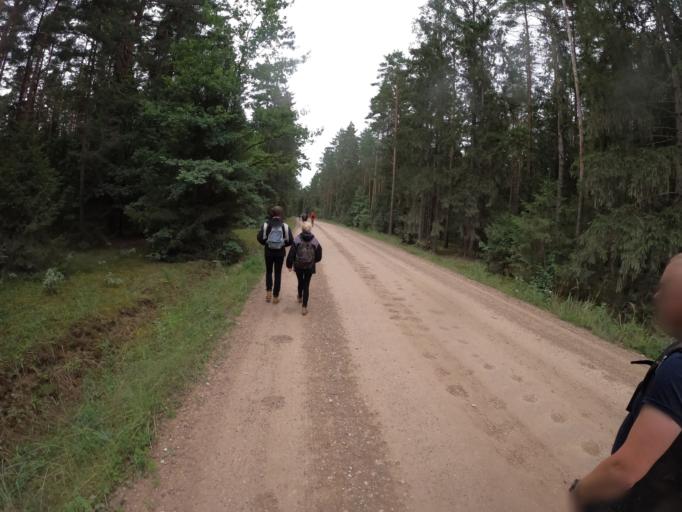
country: LV
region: Kuldigas Rajons
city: Kuldiga
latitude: 56.9892
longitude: 21.9743
